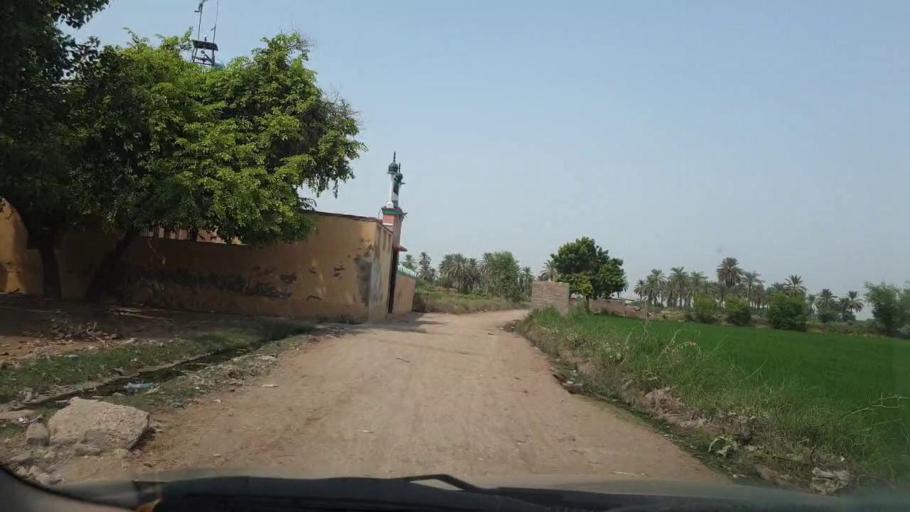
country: PK
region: Sindh
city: Larkana
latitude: 27.5895
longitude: 68.1460
